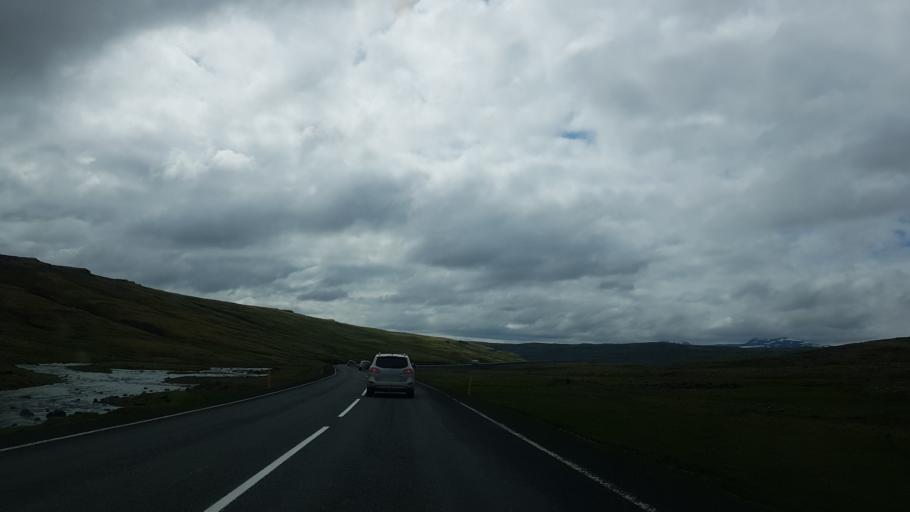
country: IS
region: West
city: Borgarnes
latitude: 64.9154
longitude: -21.1401
